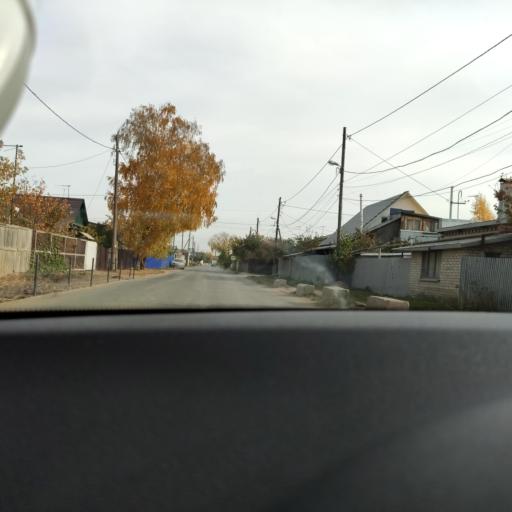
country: RU
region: Samara
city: Samara
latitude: 53.1847
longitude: 50.2303
